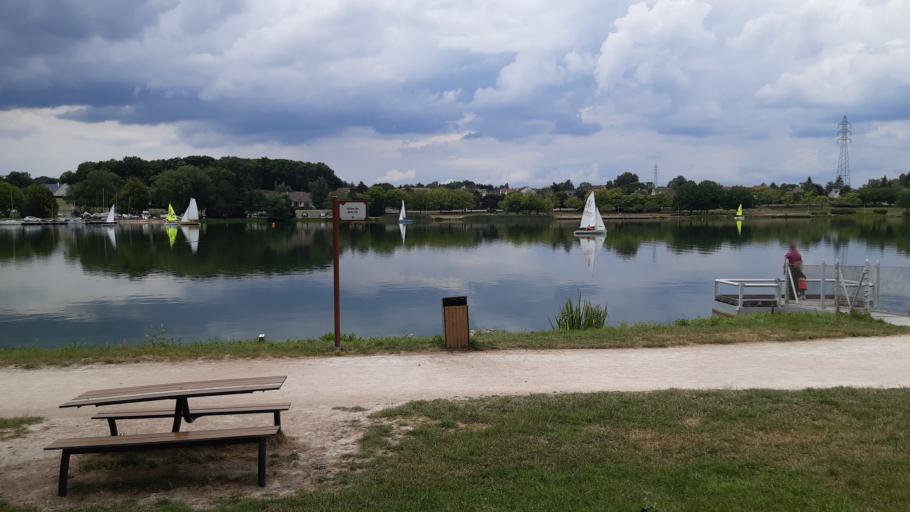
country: FR
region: Centre
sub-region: Departement d'Indre-et-Loire
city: Joue-les-Tours
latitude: 47.3544
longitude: 0.6416
